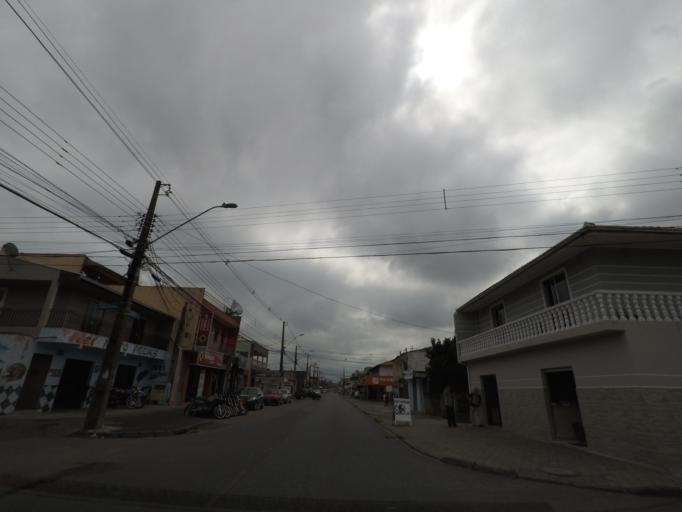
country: BR
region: Parana
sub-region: Curitiba
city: Curitiba
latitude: -25.5047
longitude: -49.3379
